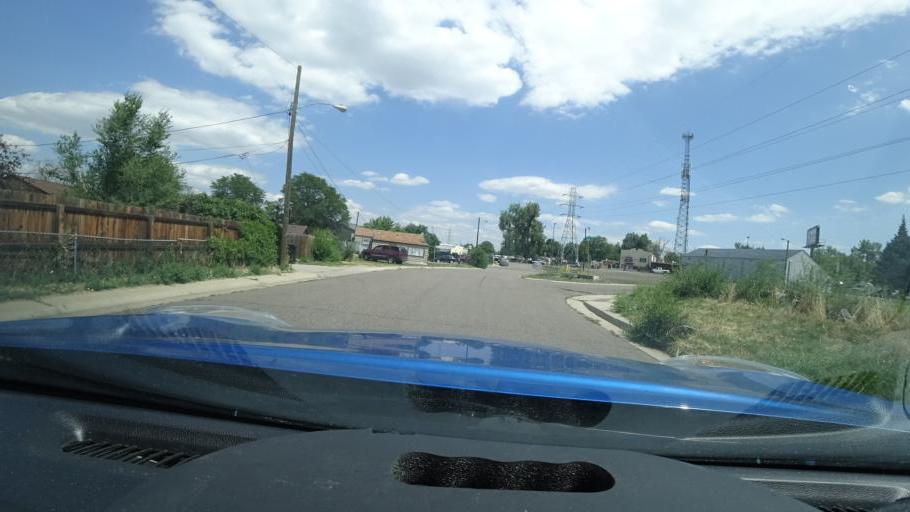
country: US
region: Colorado
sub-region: Jefferson County
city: Lakewood
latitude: 39.7018
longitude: -105.0481
